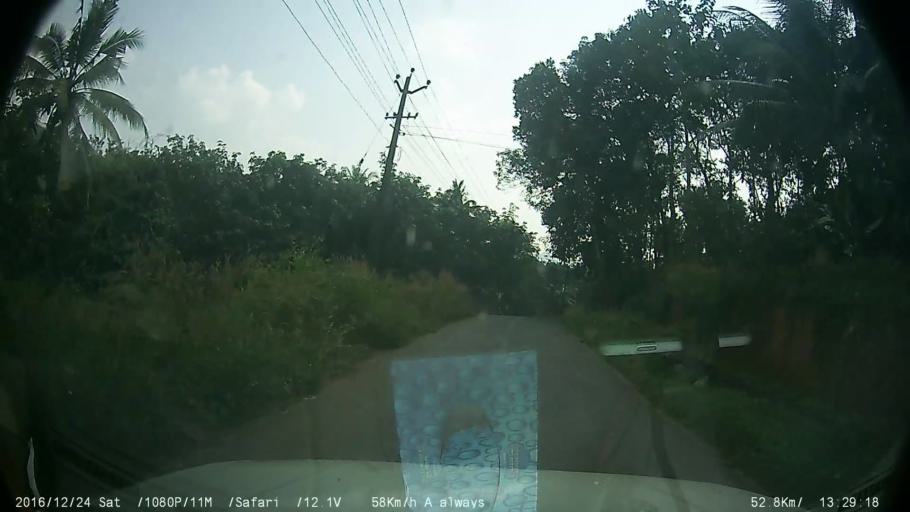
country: IN
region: Kerala
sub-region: Kottayam
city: Palackattumala
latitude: 9.8549
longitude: 76.6974
